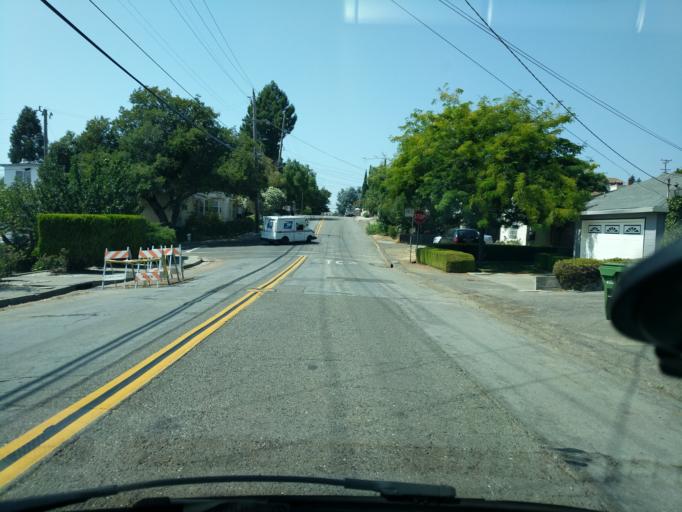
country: US
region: California
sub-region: Alameda County
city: Castro Valley
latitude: 37.7100
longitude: -122.0774
